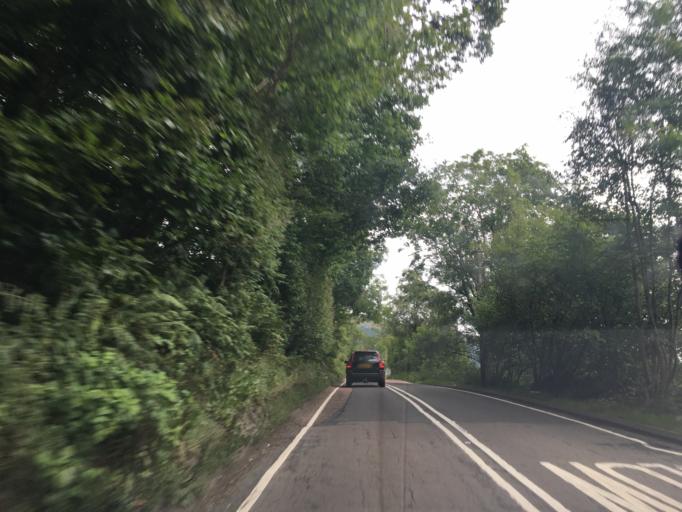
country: GB
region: Scotland
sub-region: Stirling
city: Callander
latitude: 56.3024
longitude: -4.3156
